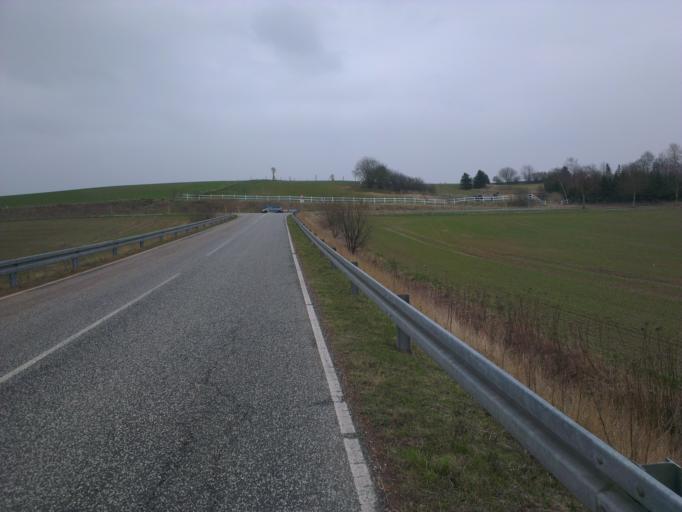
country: DK
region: Capital Region
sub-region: Frederikssund Kommune
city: Slangerup
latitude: 55.8324
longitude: 12.1839
